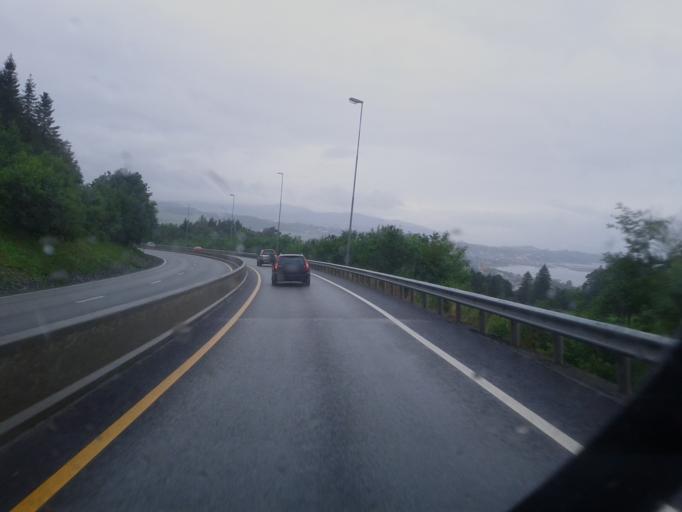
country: NO
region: Sor-Trondelag
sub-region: Malvik
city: Malvik
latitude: 63.4257
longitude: 10.5694
